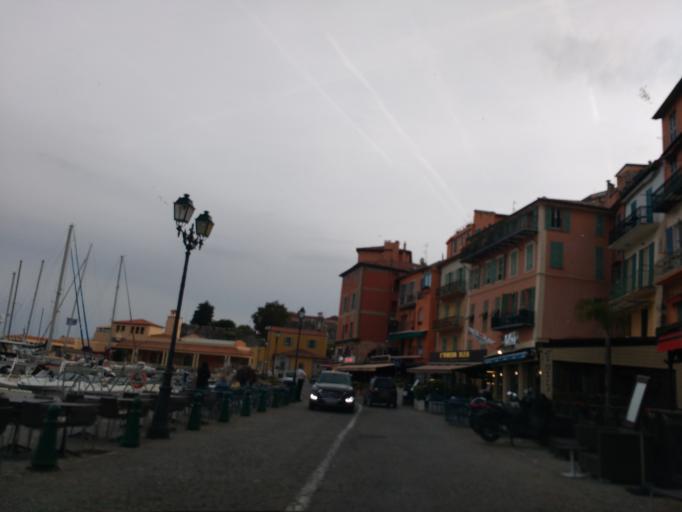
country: FR
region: Provence-Alpes-Cote d'Azur
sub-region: Departement des Alpes-Maritimes
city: Villefranche-sur-Mer
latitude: 43.7041
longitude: 7.3124
